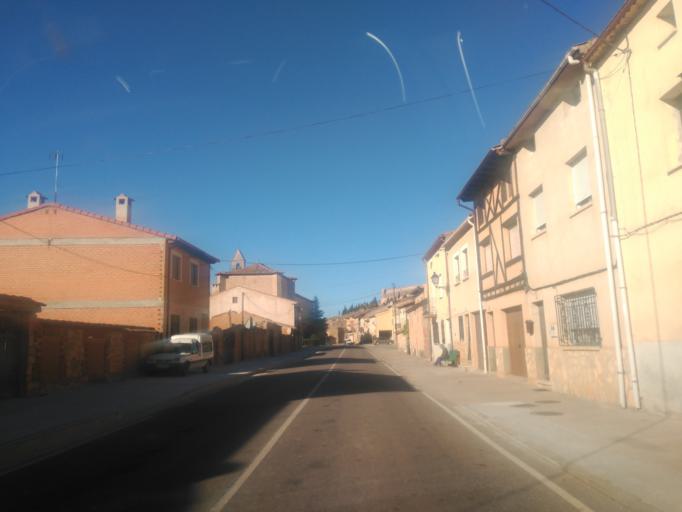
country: ES
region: Castille and Leon
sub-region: Provincia de Burgos
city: Penaranda de Duero
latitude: 41.6898
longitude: -3.4757
